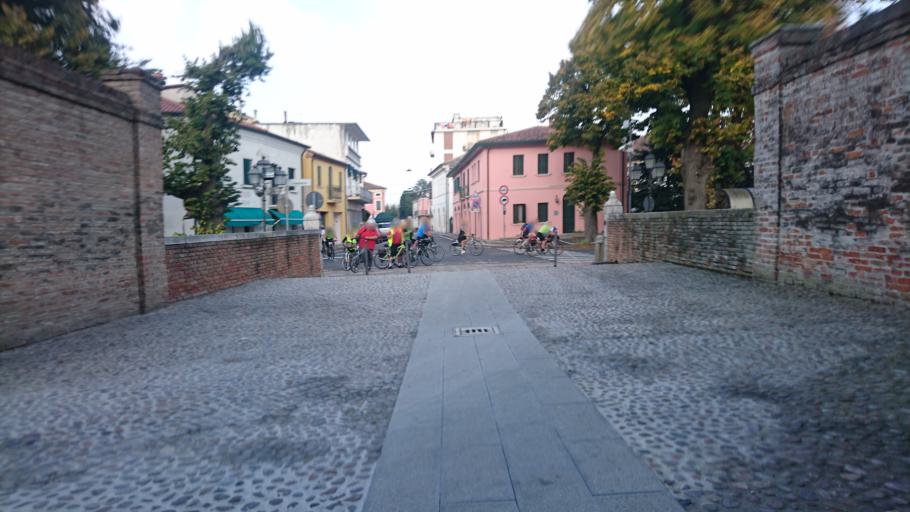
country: IT
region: Veneto
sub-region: Provincia di Rovigo
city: Arqua Polesine
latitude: 45.0097
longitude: 11.7403
